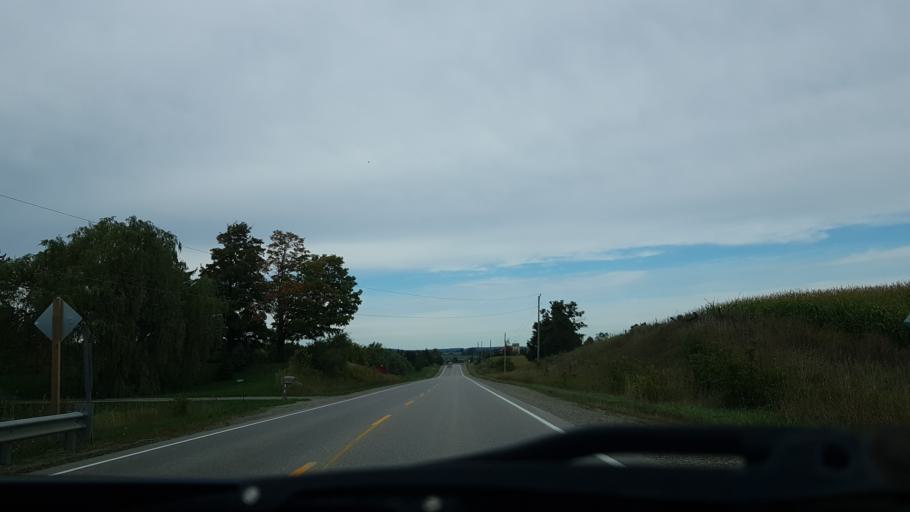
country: CA
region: Ontario
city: Shelburne
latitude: 44.1076
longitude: -80.0251
